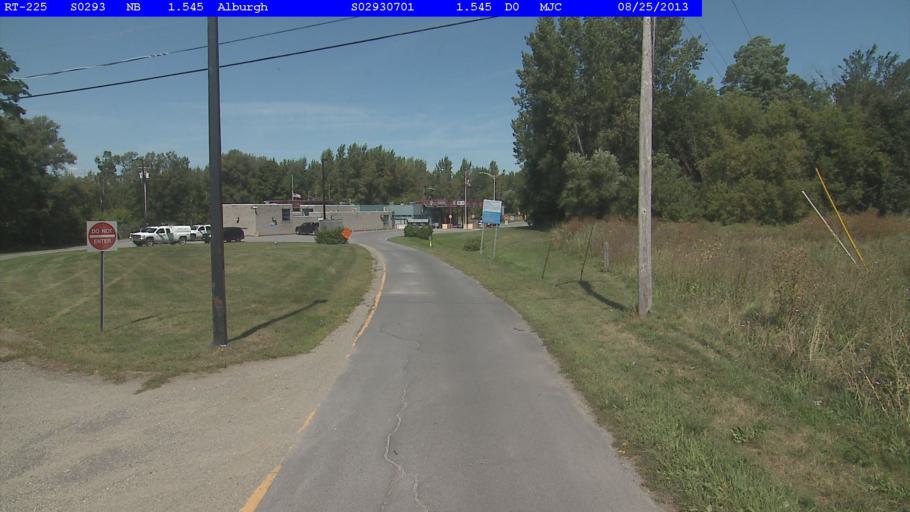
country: US
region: New York
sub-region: Clinton County
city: Rouses Point
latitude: 45.0107
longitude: -73.2959
